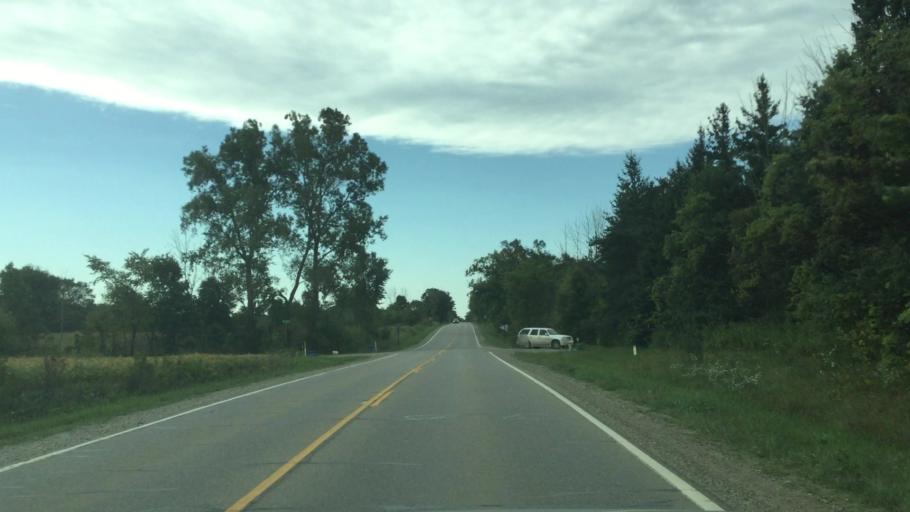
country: US
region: Michigan
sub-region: Livingston County
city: Howell
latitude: 42.6452
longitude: -83.8760
